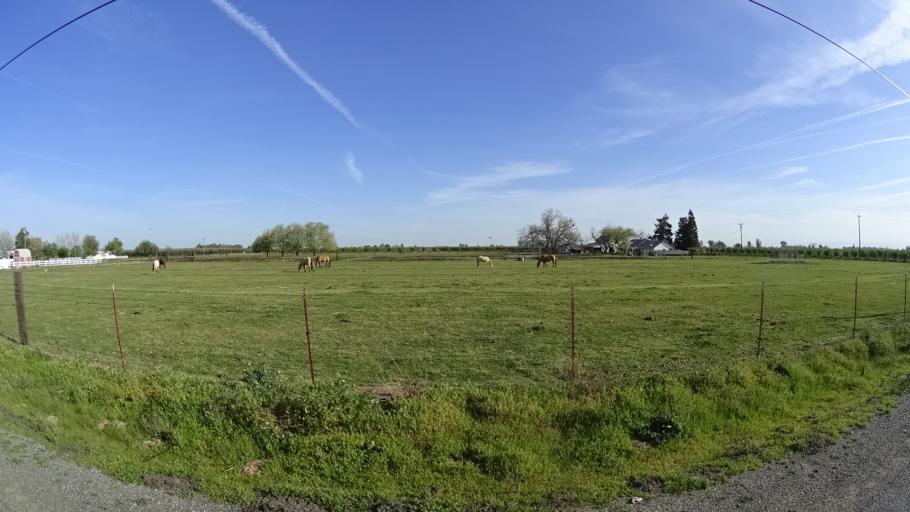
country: US
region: California
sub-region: Glenn County
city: Orland
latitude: 39.7187
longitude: -122.2332
